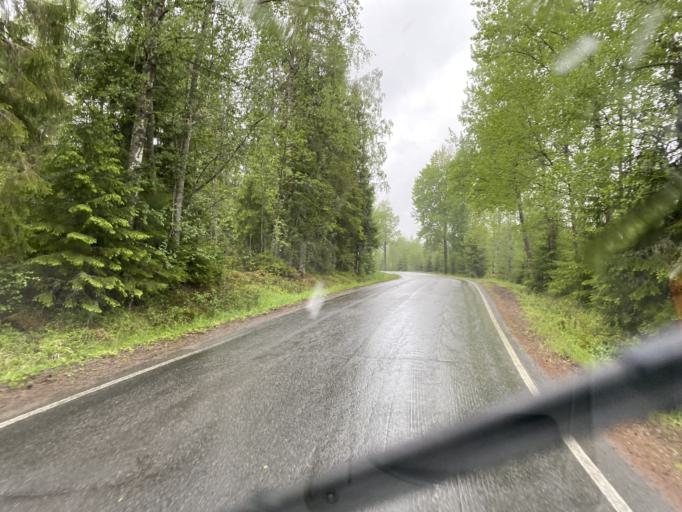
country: FI
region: Haeme
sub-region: Forssa
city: Humppila
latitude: 61.0922
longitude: 23.3153
